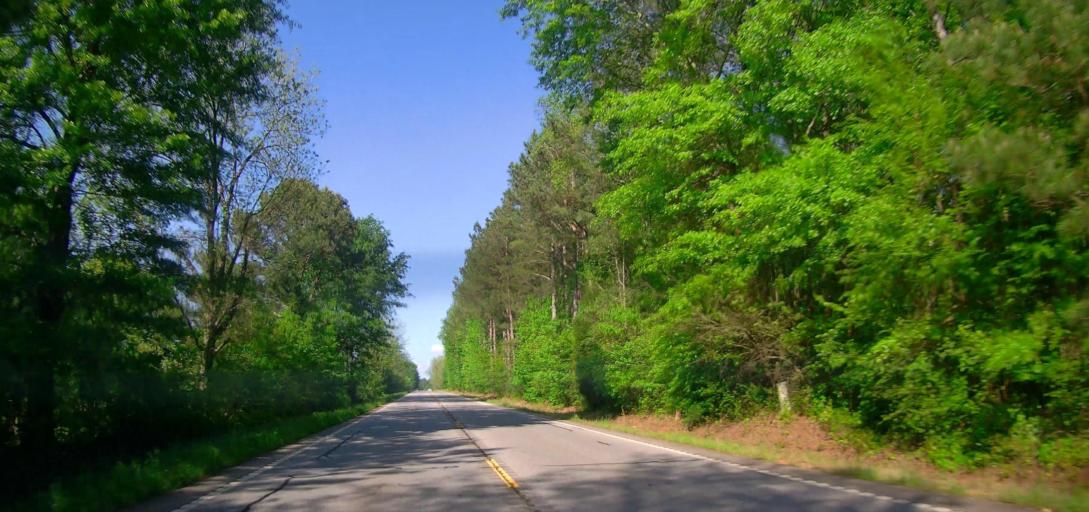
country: US
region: Georgia
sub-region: Morgan County
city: Madison
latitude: 33.5455
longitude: -83.5080
